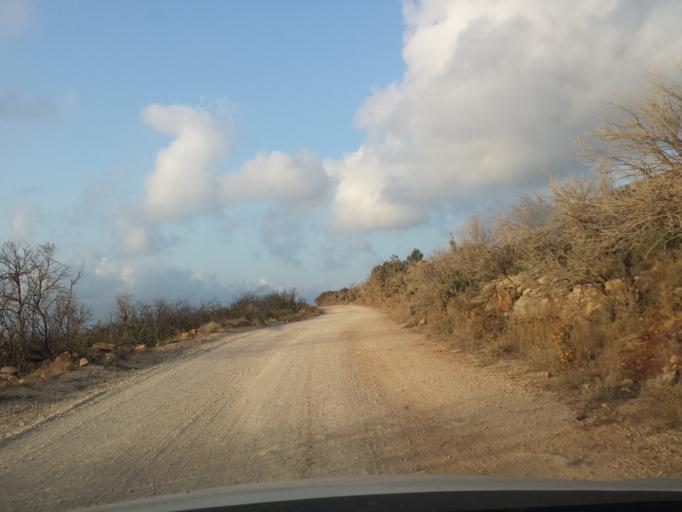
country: GR
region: Peloponnese
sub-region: Nomos Messinias
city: Pylos
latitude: 36.8906
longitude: 21.6882
